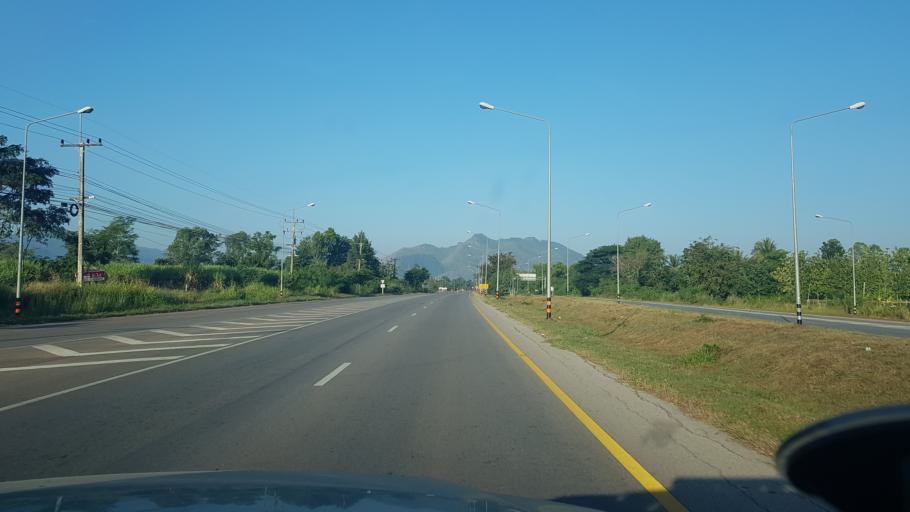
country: TH
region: Chaiyaphum
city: Khon San
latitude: 16.5956
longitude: 101.9216
